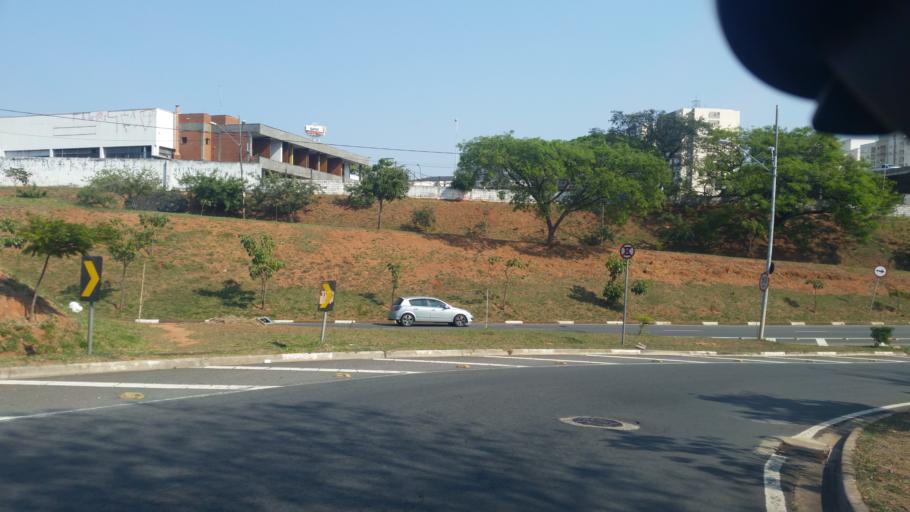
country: BR
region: Sao Paulo
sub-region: Campinas
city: Campinas
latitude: -22.9047
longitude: -47.0736
